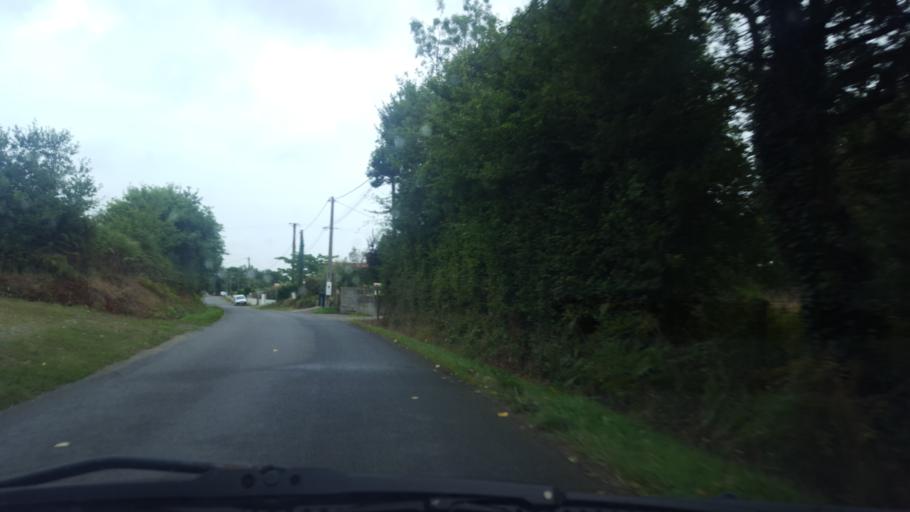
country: FR
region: Pays de la Loire
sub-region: Departement de la Loire-Atlantique
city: Saint-Lumine-de-Coutais
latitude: 47.0538
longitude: -1.7179
